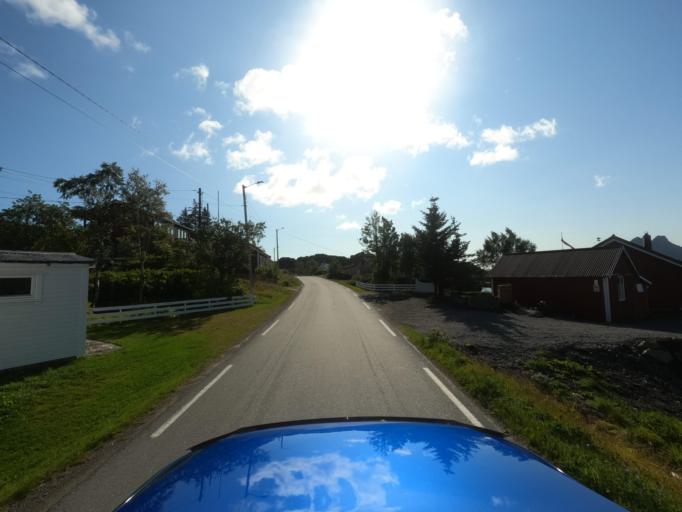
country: NO
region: Nordland
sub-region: Vestvagoy
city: Evjen
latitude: 68.1202
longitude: 13.7823
